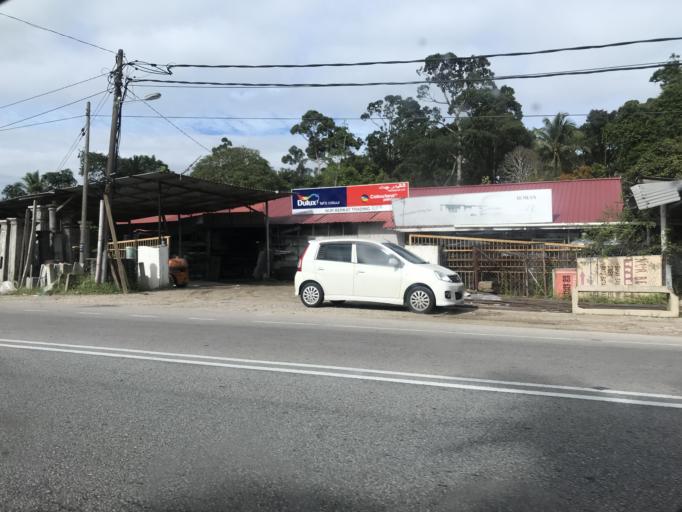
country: MY
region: Kelantan
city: Kota Bharu
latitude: 6.1304
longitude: 102.1781
